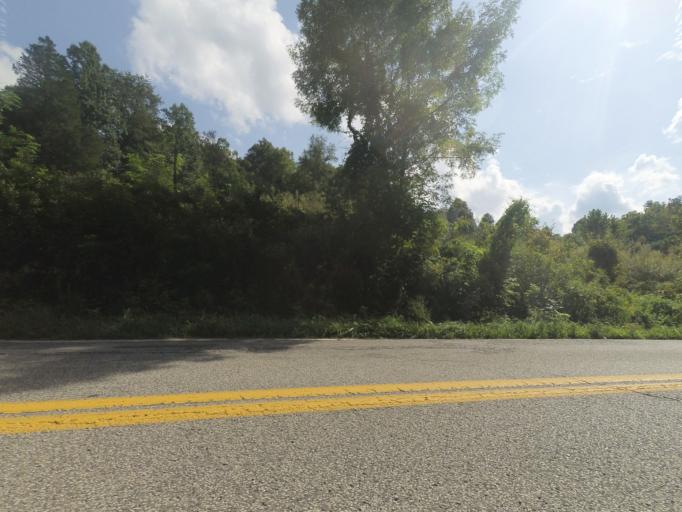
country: US
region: West Virginia
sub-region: Wayne County
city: Ceredo
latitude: 38.3714
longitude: -82.5500
